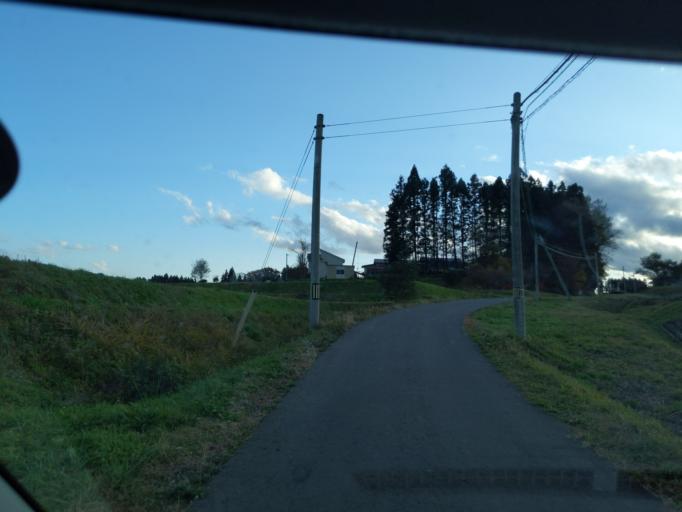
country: JP
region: Iwate
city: Mizusawa
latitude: 39.0938
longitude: 141.0387
